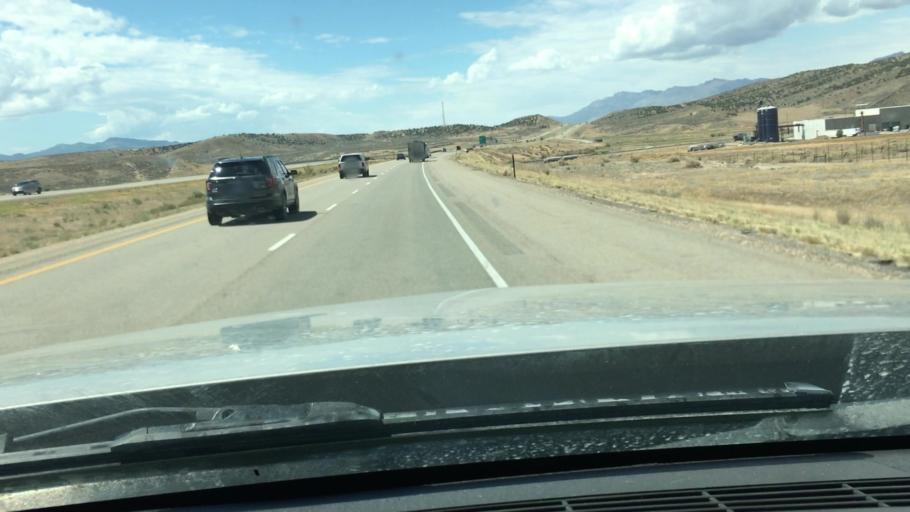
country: US
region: Utah
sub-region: Juab County
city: Nephi
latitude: 39.4909
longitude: -111.9724
